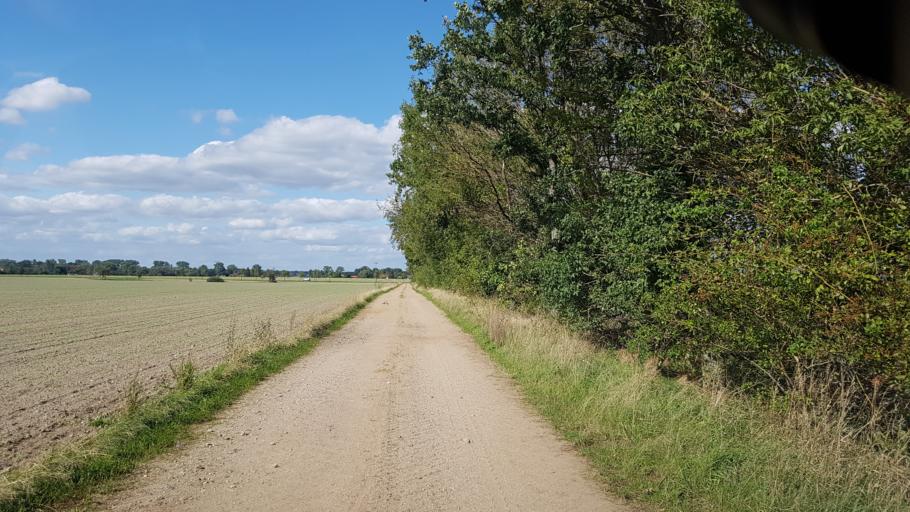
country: DE
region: Brandenburg
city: Sonnewalde
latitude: 51.6910
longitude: 13.6628
